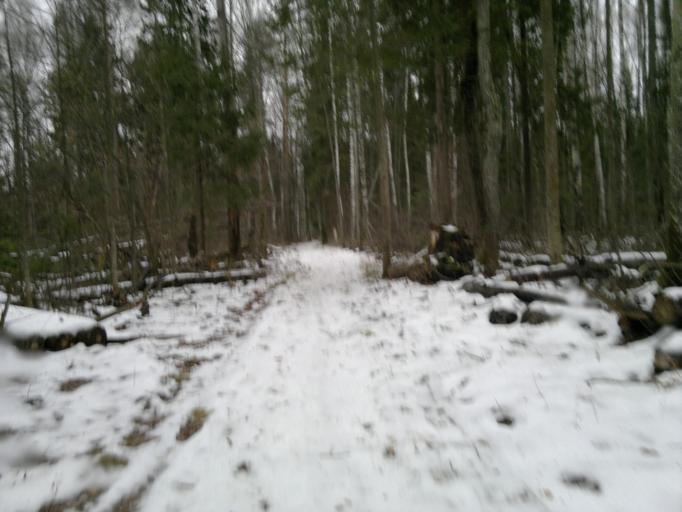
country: RU
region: Mariy-El
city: Yoshkar-Ola
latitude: 56.6089
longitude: 47.9570
